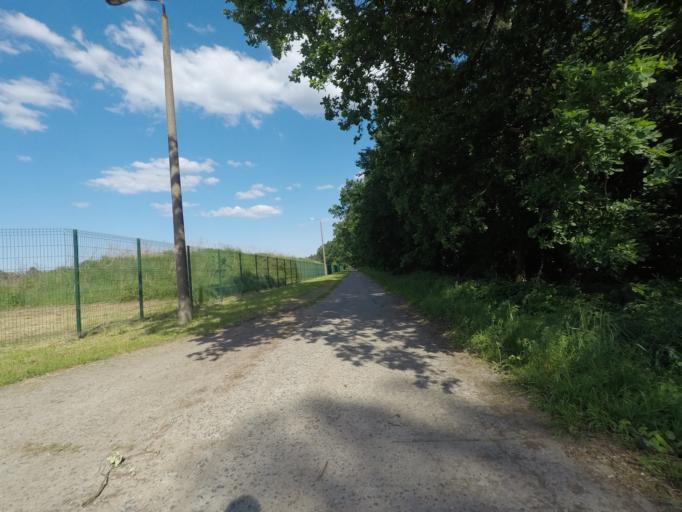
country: DE
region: Brandenburg
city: Britz
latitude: 52.8684
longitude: 13.7784
